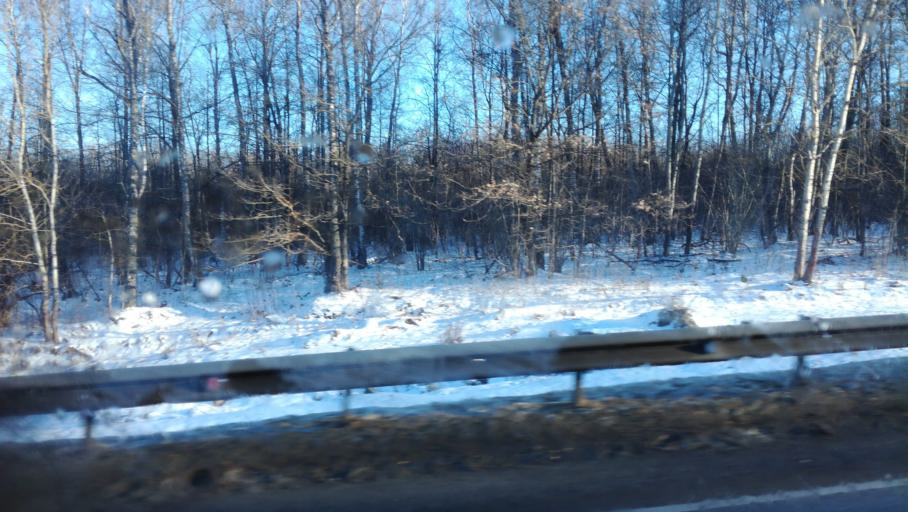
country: RU
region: Tula
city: Kosaya Gora
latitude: 54.1655
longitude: 37.4627
